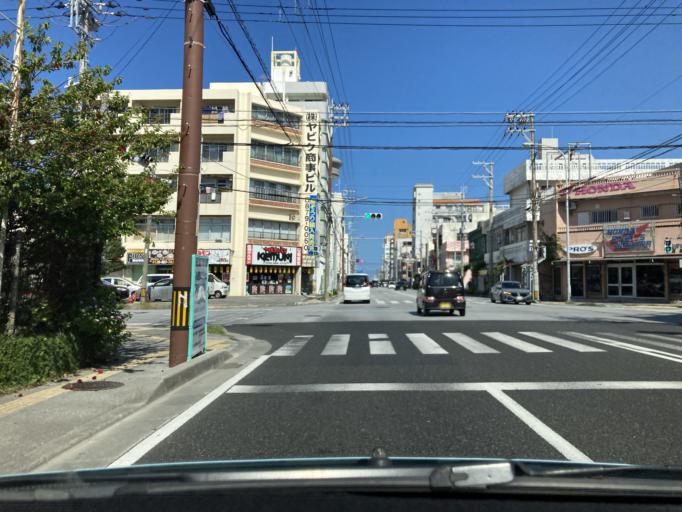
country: JP
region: Okinawa
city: Naha-shi
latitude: 26.2385
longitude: 127.6816
